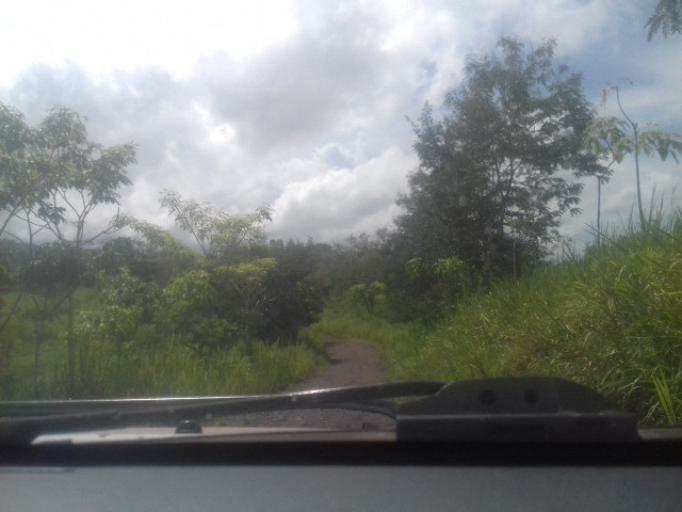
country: NI
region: Jinotega
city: San Jose de Bocay
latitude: 13.5040
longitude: -85.2373
